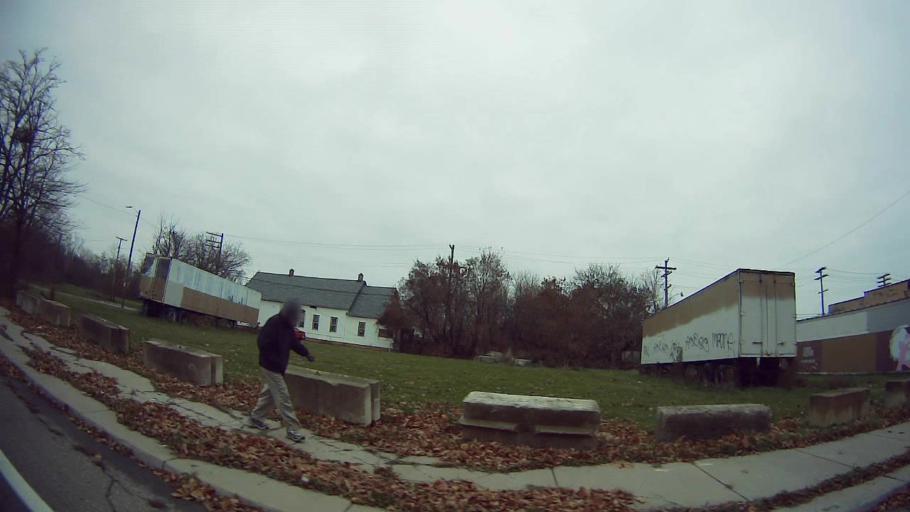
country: US
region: Michigan
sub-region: Wayne County
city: Detroit
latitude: 42.3620
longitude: -83.0427
